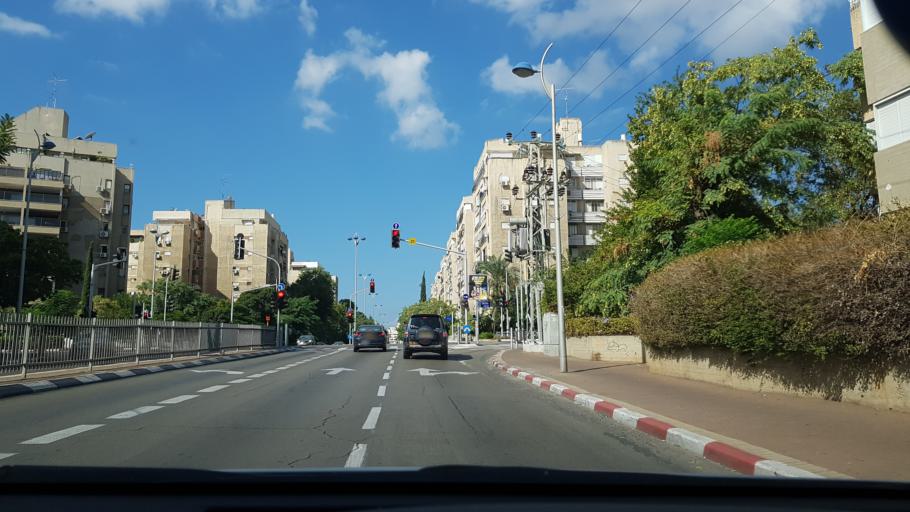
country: IL
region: Tel Aviv
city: Holon
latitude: 32.0100
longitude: 34.7930
